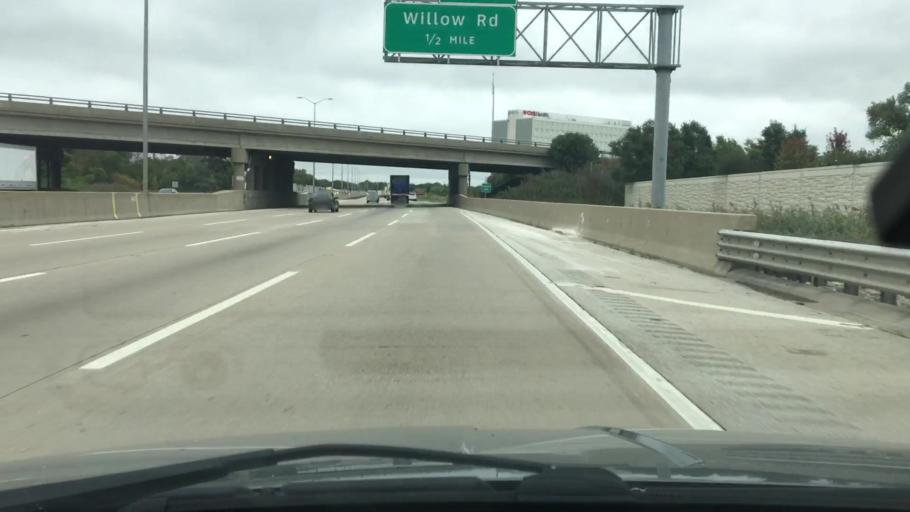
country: US
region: Illinois
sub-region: Cook County
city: Northbrook
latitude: 42.1172
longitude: -87.8788
